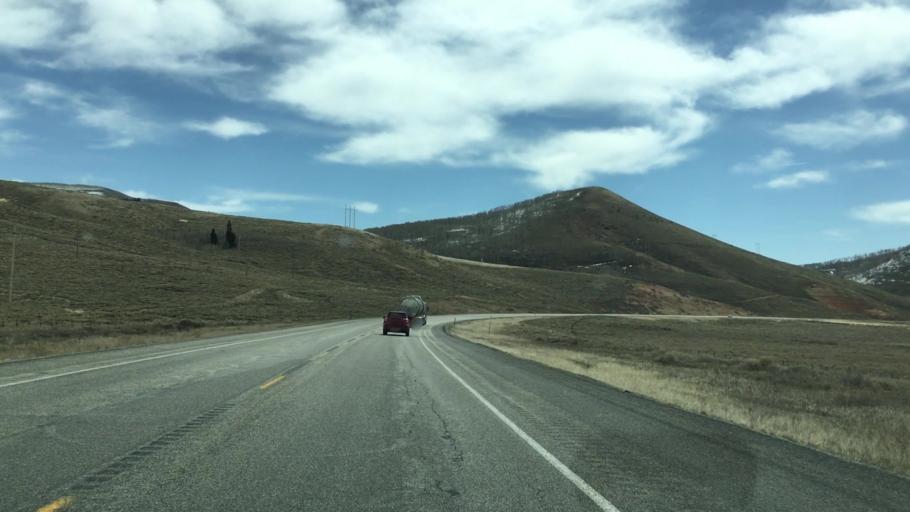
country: US
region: Utah
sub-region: Wasatch County
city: Heber
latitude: 40.2254
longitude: -111.1097
